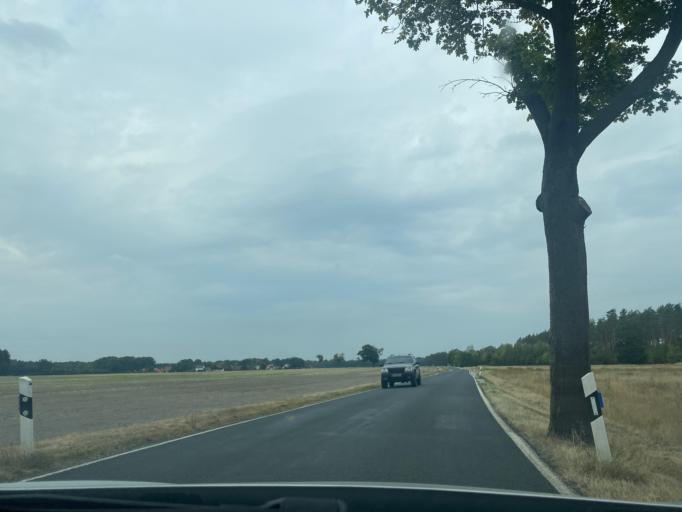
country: DE
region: Saxony
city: Konigswartha
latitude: 51.3057
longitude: 14.3810
